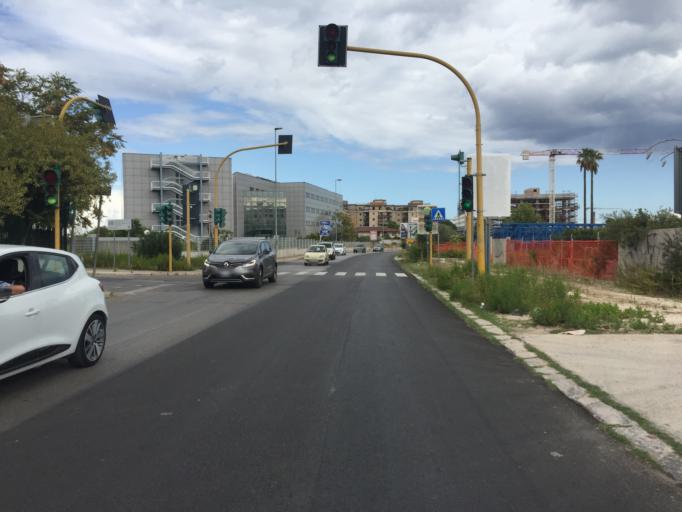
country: IT
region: Apulia
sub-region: Provincia di Bari
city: Bari
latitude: 41.1052
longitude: 16.8503
